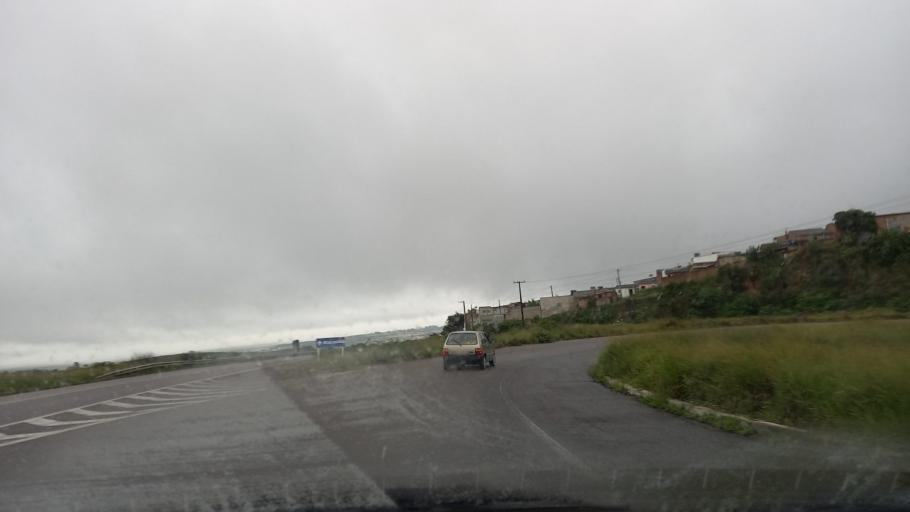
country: BR
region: Pernambuco
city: Garanhuns
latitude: -8.8765
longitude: -36.5063
